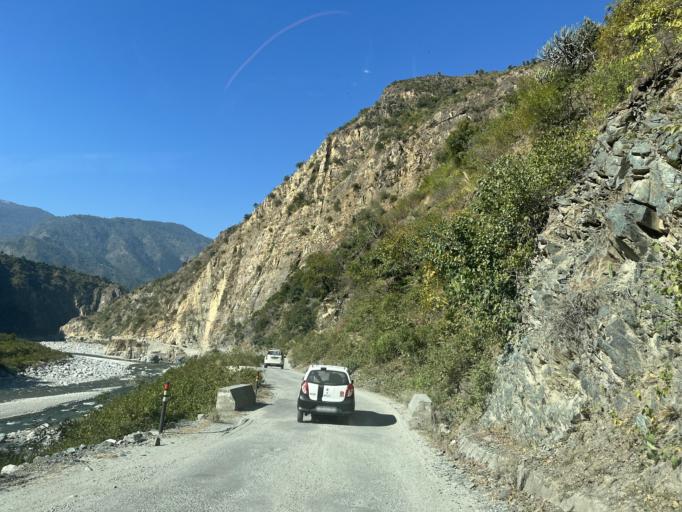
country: IN
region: Uttarakhand
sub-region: Naini Tal
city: Naini Tal
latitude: 29.5079
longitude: 79.4617
